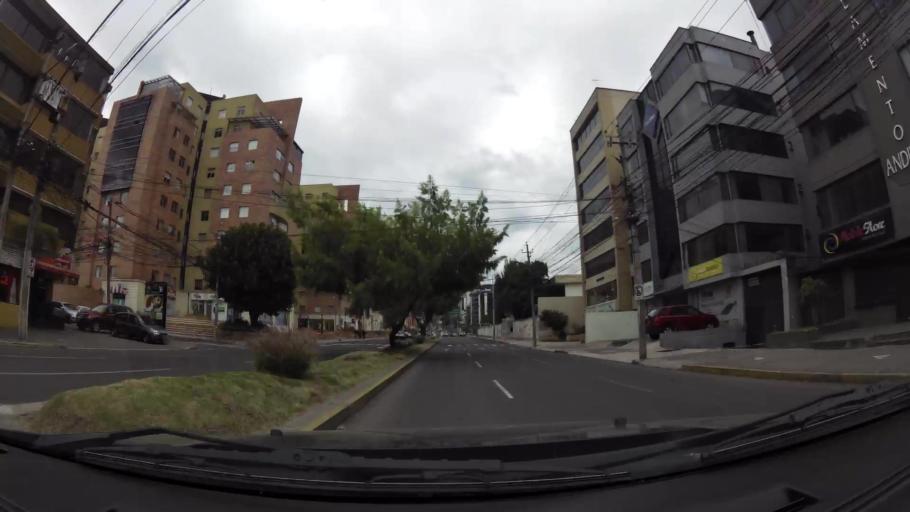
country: EC
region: Pichincha
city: Quito
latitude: -0.1706
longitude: -78.4782
